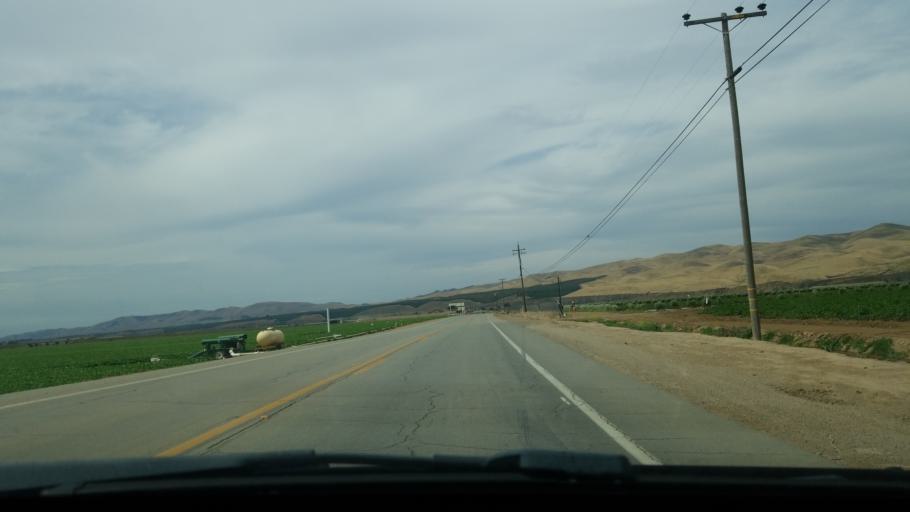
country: US
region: California
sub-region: Santa Barbara County
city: Santa Maria
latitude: 34.9121
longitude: -120.3478
